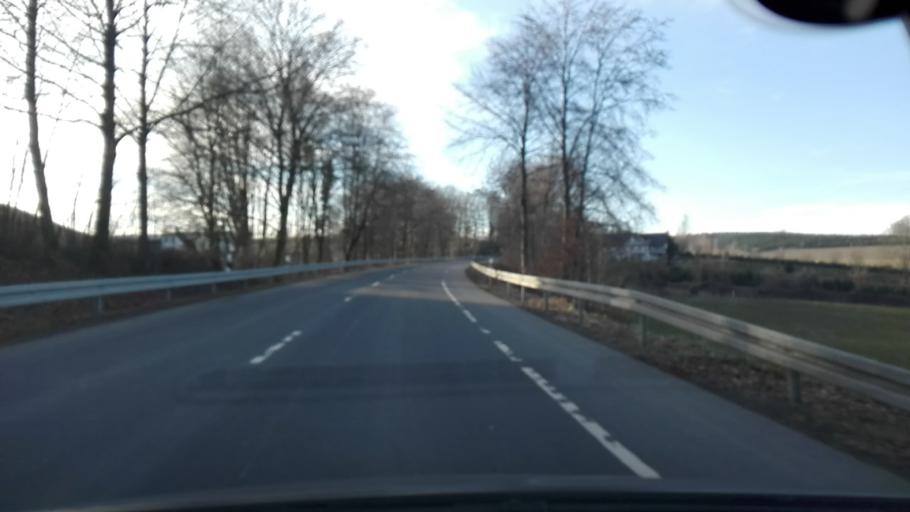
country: DE
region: North Rhine-Westphalia
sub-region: Regierungsbezirk Arnsberg
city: Schmallenberg
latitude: 51.1642
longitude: 8.2110
